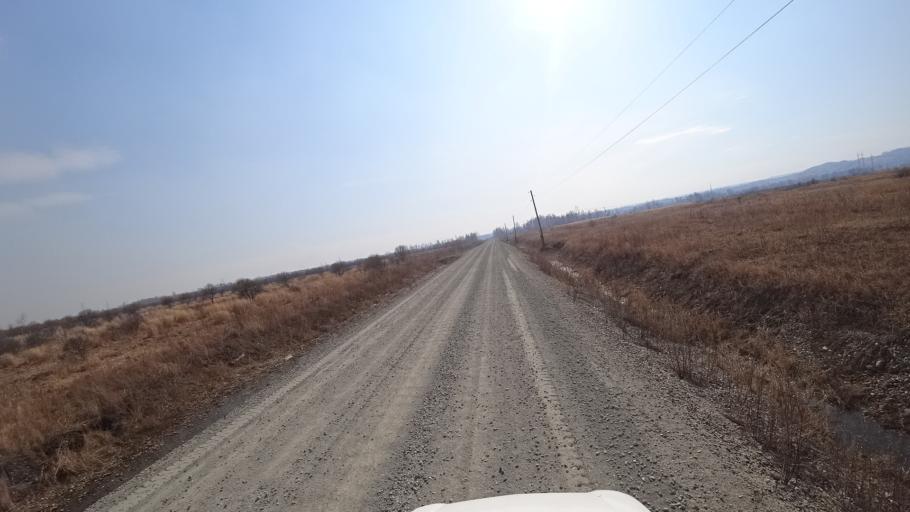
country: RU
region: Amur
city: Novobureyskiy
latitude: 49.8086
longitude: 129.9671
